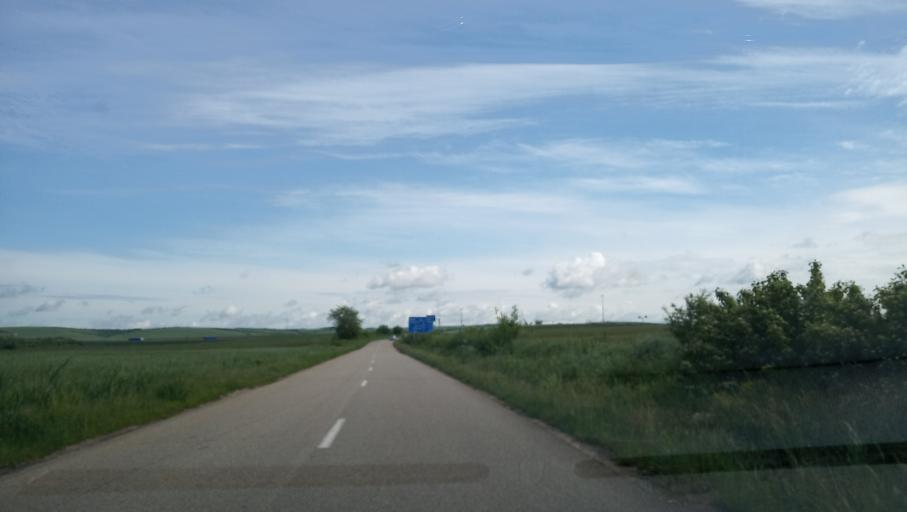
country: RO
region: Timis
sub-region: Comuna Topolovatu Mare
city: Topolovatu Mare
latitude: 45.7930
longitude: 21.6544
